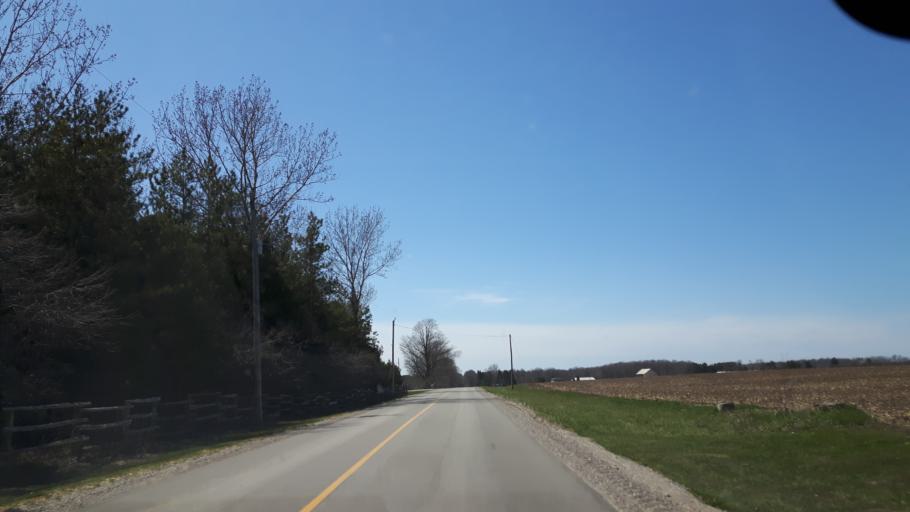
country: CA
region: Ontario
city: Bluewater
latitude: 43.5800
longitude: -81.6543
